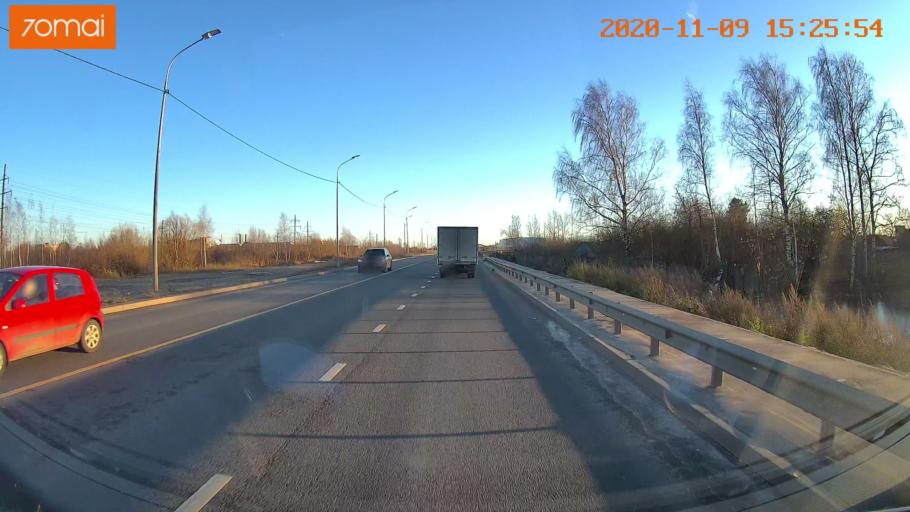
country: RU
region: Ivanovo
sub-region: Gorod Ivanovo
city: Ivanovo
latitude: 56.9799
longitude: 40.9170
